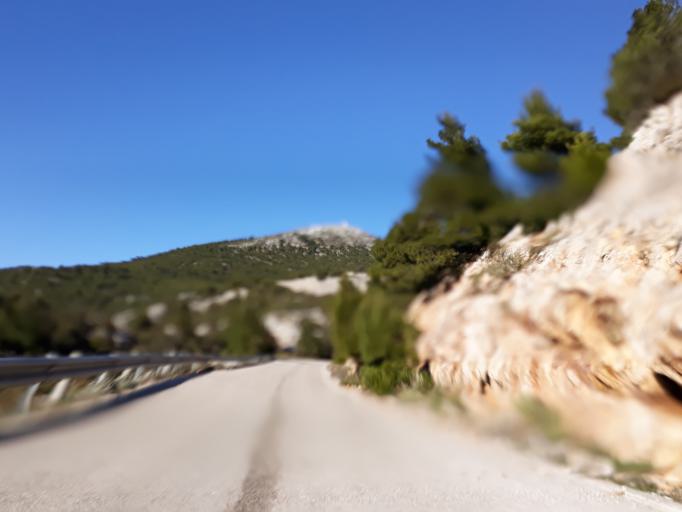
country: GR
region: Attica
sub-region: Nomarchia Dytikis Attikis
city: Fyli
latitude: 38.1389
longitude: 23.6480
